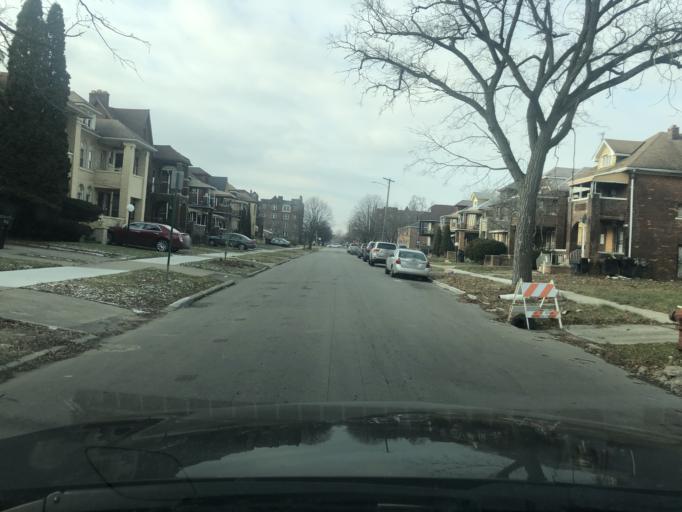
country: US
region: Michigan
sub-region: Wayne County
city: Highland Park
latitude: 42.3920
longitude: -83.1301
